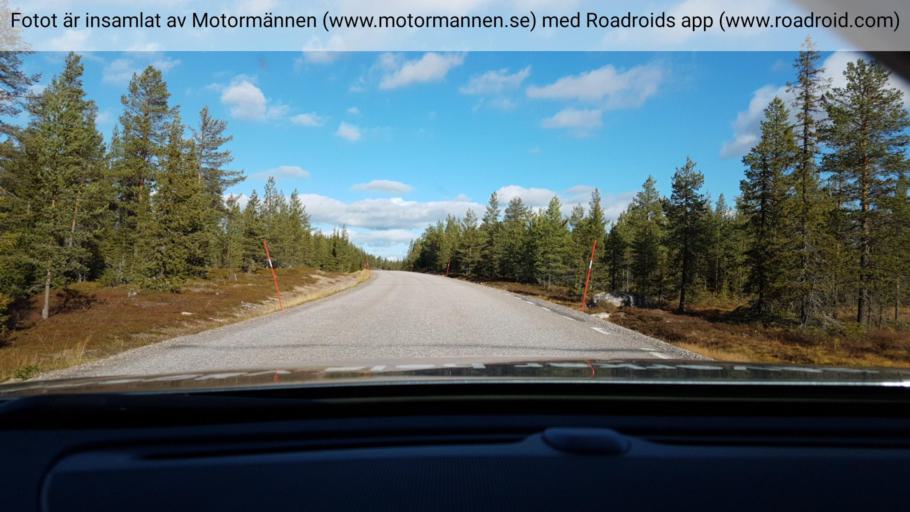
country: SE
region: Norrbotten
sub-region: Arjeplogs Kommun
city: Arjeplog
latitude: 65.8567
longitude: 18.4058
